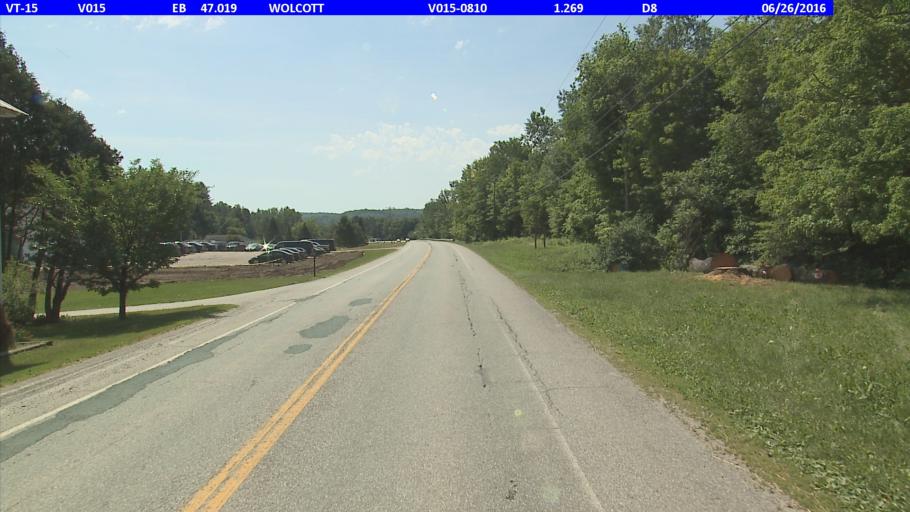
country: US
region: Vermont
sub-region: Lamoille County
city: Morrisville
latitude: 44.5705
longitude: -72.5061
